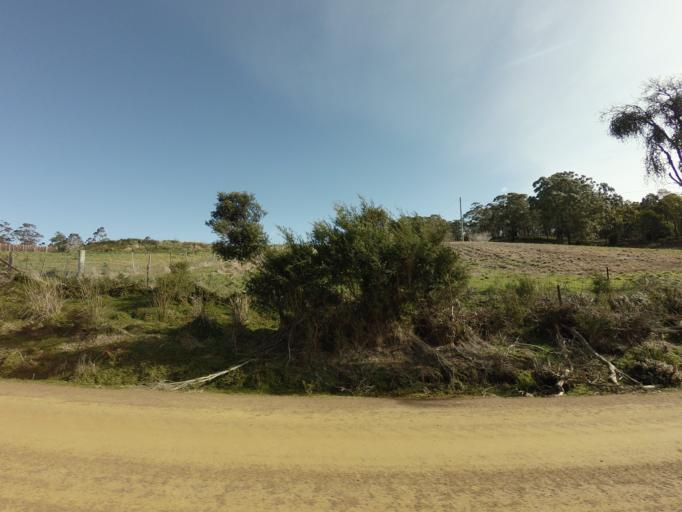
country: AU
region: Tasmania
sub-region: Kingborough
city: Kettering
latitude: -43.0875
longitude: 147.2644
